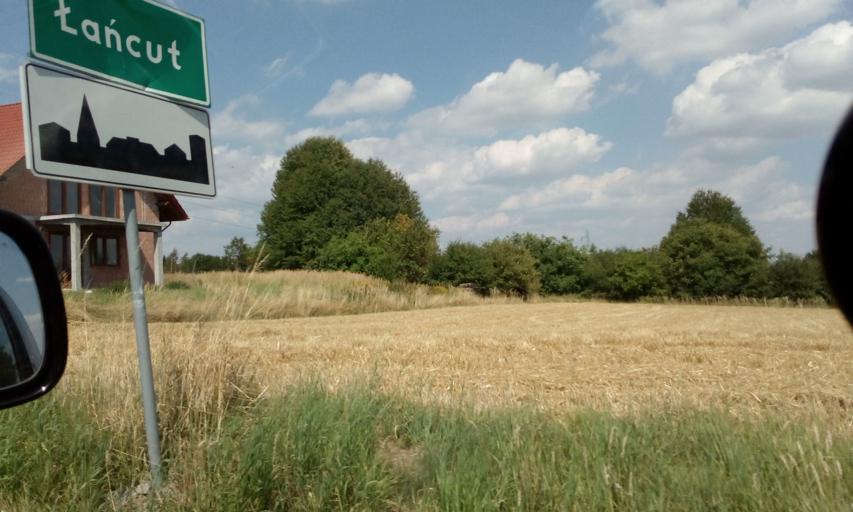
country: PL
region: Subcarpathian Voivodeship
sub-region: Powiat lancucki
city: Lancut
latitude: 50.0536
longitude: 22.2349
